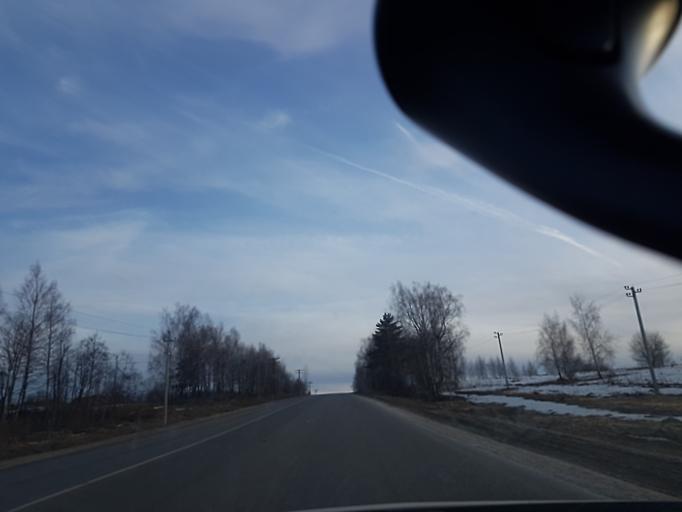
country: RU
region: Moskovskaya
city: Istra
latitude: 55.8824
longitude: 36.8584
